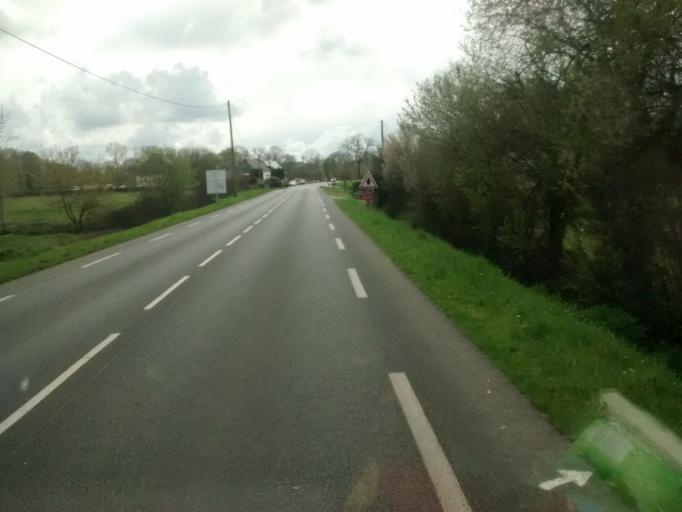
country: FR
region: Brittany
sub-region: Departement du Morbihan
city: Malestroit
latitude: 47.8250
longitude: -2.3798
